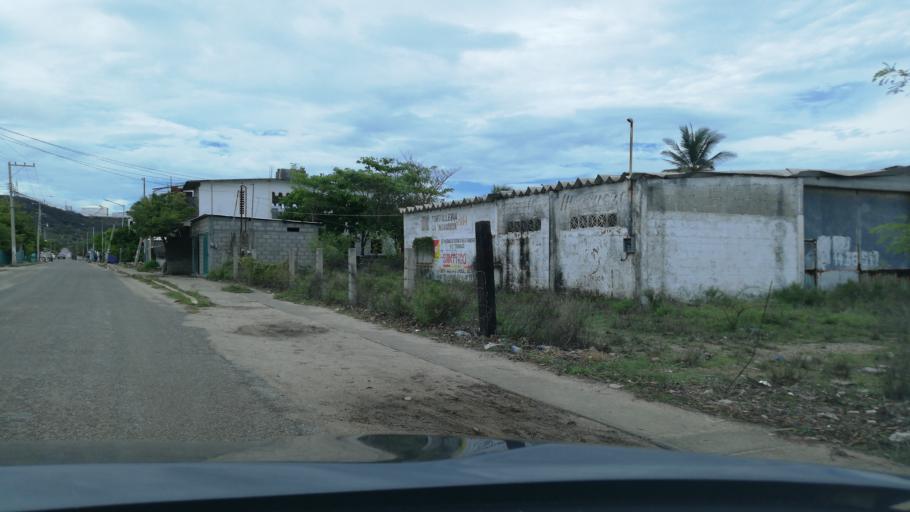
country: MX
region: Oaxaca
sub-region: Salina Cruz
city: Salina Cruz
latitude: 16.1630
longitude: -95.2221
